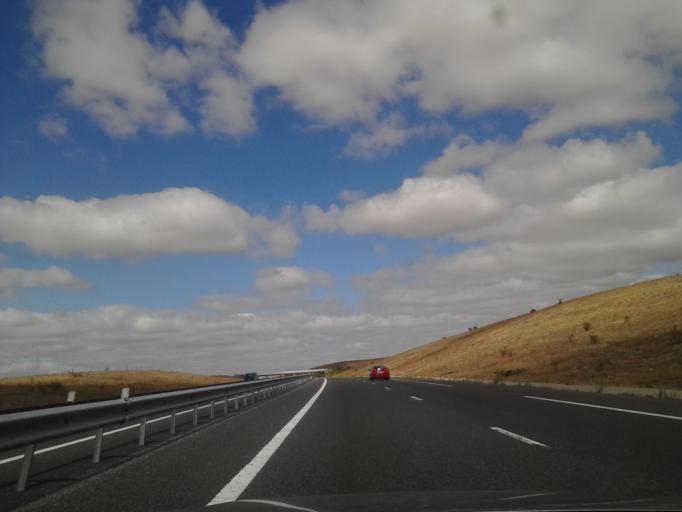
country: FR
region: Midi-Pyrenees
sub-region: Departement de l'Aveyron
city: La Cavalerie
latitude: 44.0264
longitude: 3.1132
